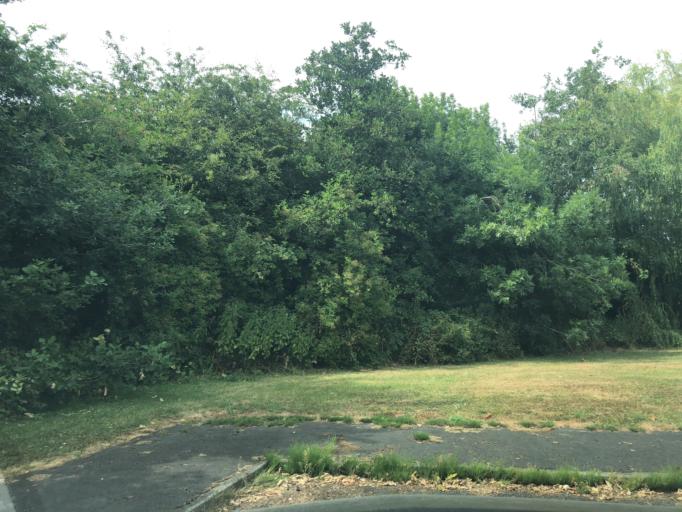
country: GB
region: England
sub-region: North Yorkshire
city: Stokesley
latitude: 54.4736
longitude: -1.1946
